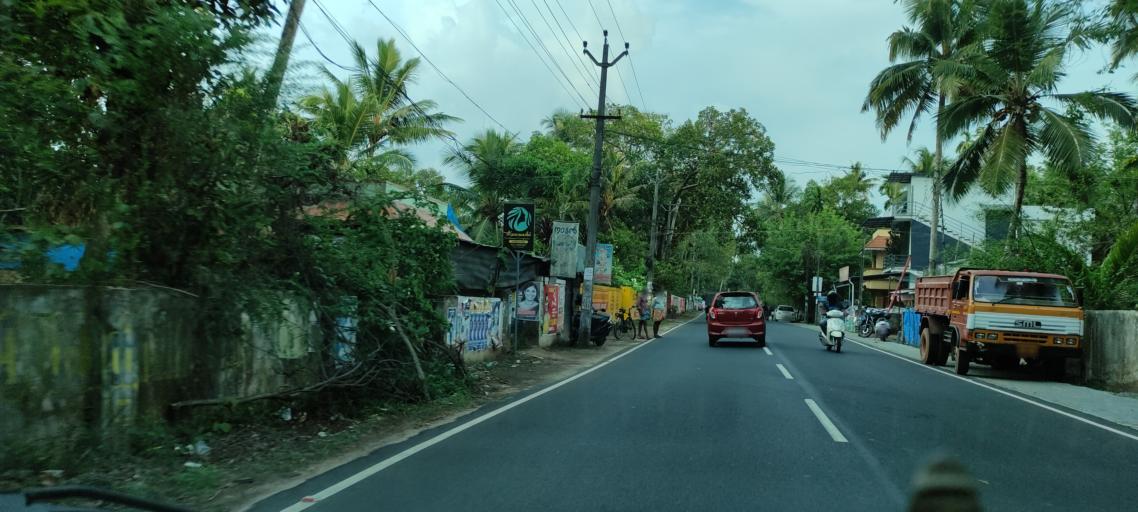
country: IN
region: Kerala
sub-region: Alappuzha
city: Arukutti
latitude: 9.8392
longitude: 76.3316
